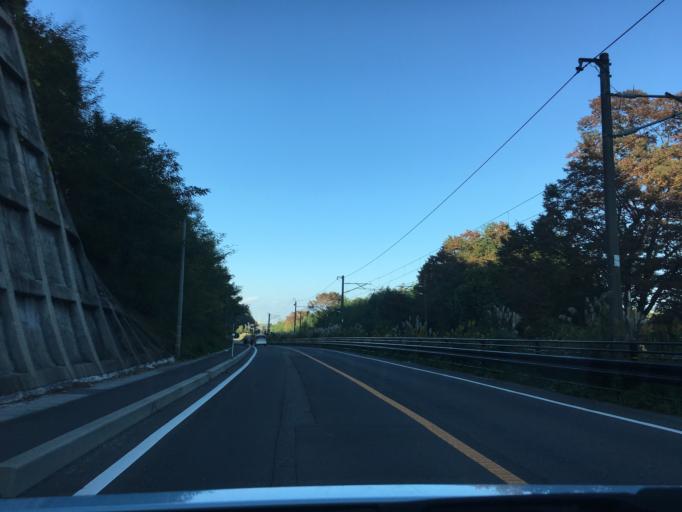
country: JP
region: Fukushima
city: Sukagawa
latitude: 37.3121
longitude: 140.3777
